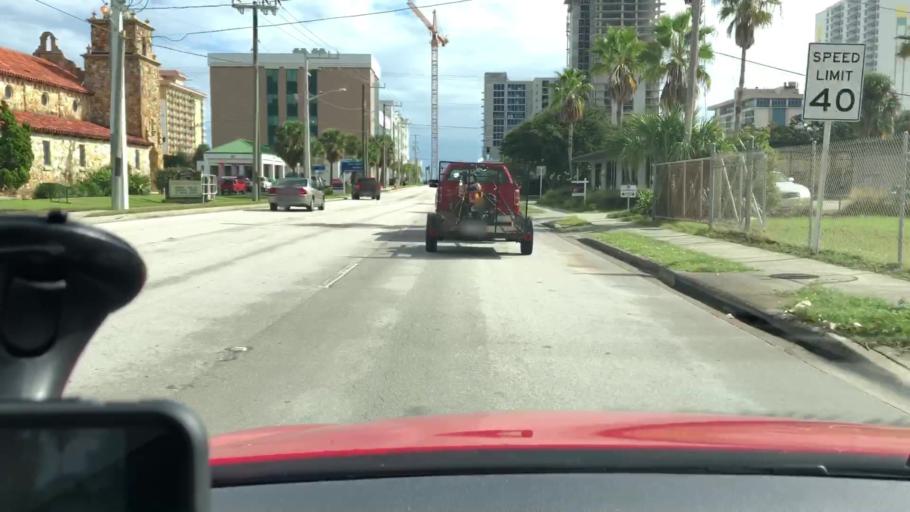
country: US
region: Florida
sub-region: Volusia County
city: Daytona Beach
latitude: 29.2329
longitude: -81.0145
